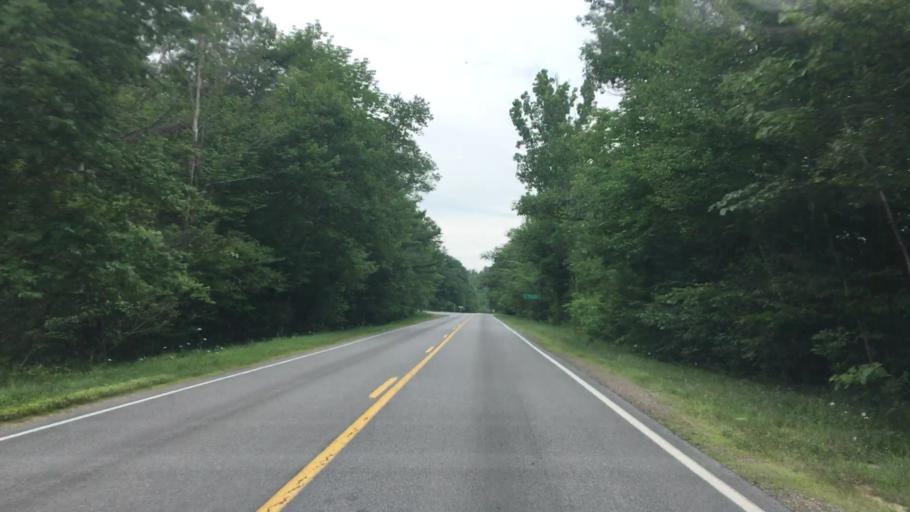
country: US
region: New York
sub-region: Essex County
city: Keeseville
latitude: 44.4820
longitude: -73.5961
